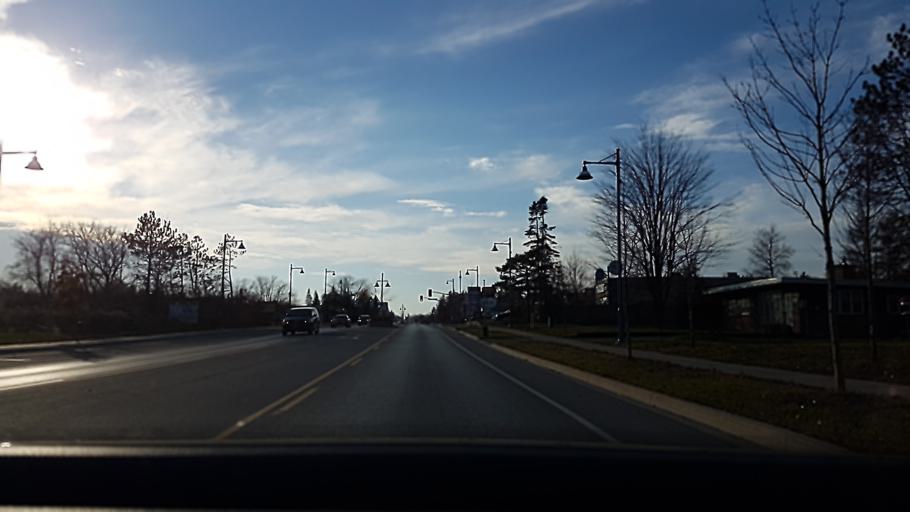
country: CA
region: Ontario
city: Innisfil
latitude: 44.3143
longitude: -79.5509
